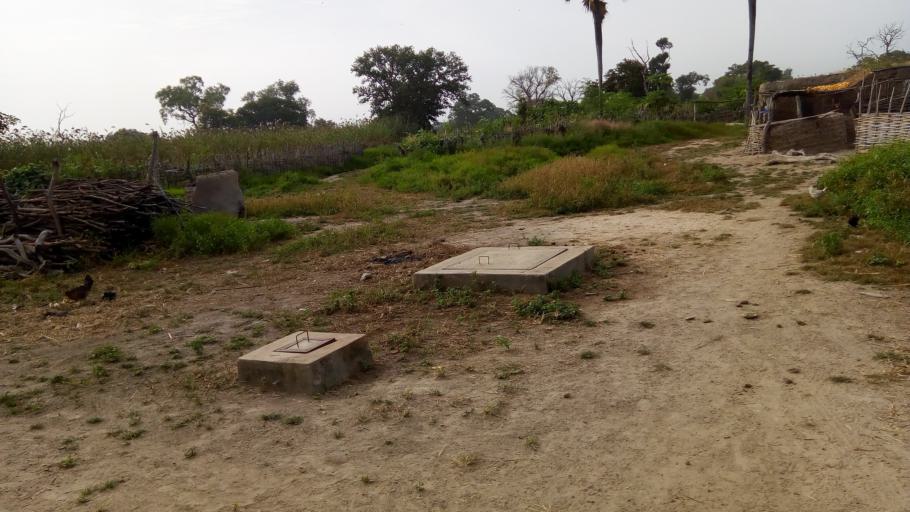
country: ML
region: Kayes
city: Kita
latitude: 13.1915
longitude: -8.8199
